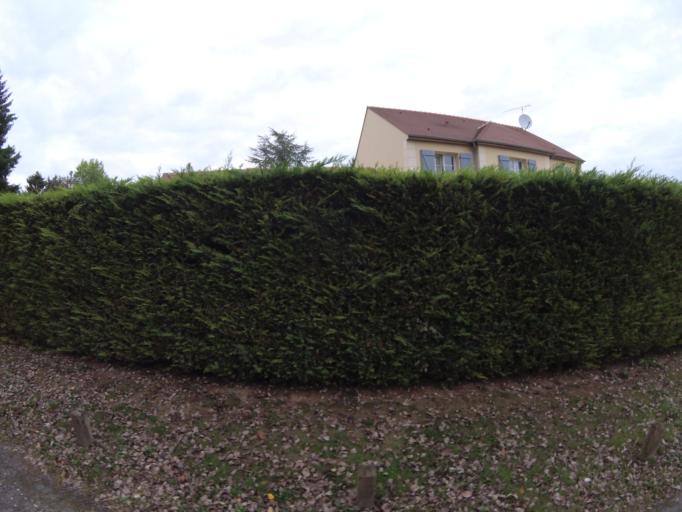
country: FR
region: Ile-de-France
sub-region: Departement de Seine-et-Marne
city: Collegien
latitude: 48.8424
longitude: 2.6742
